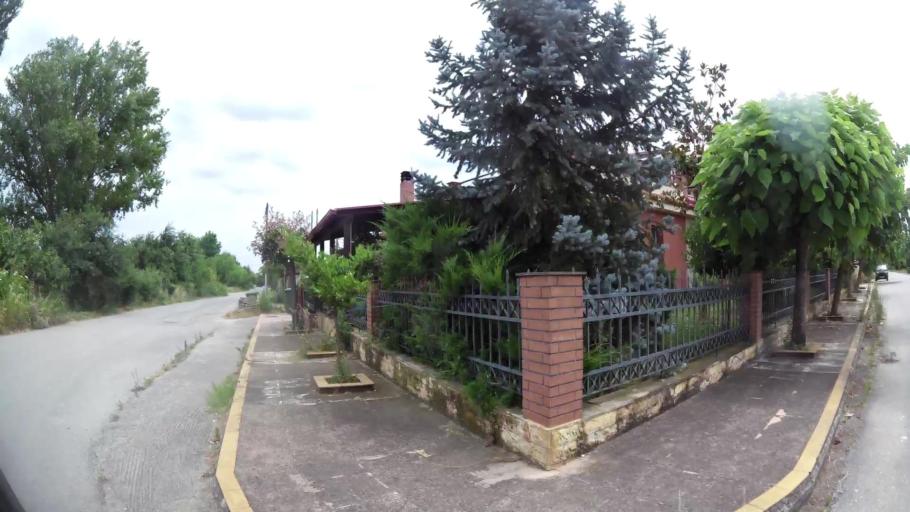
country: GR
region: Central Macedonia
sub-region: Nomos Pierias
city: Kallithea
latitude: 40.2768
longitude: 22.5714
